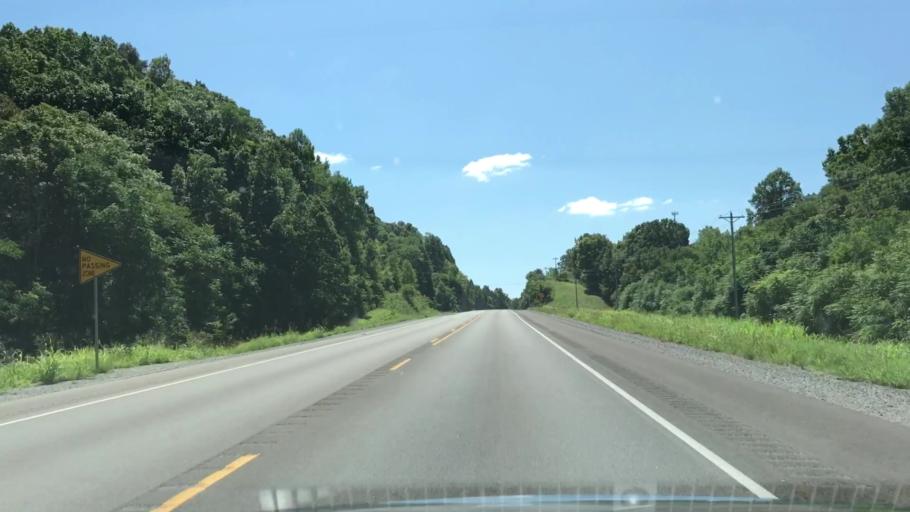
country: US
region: Kentucky
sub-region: Cumberland County
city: Burkesville
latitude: 36.7191
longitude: -85.3658
